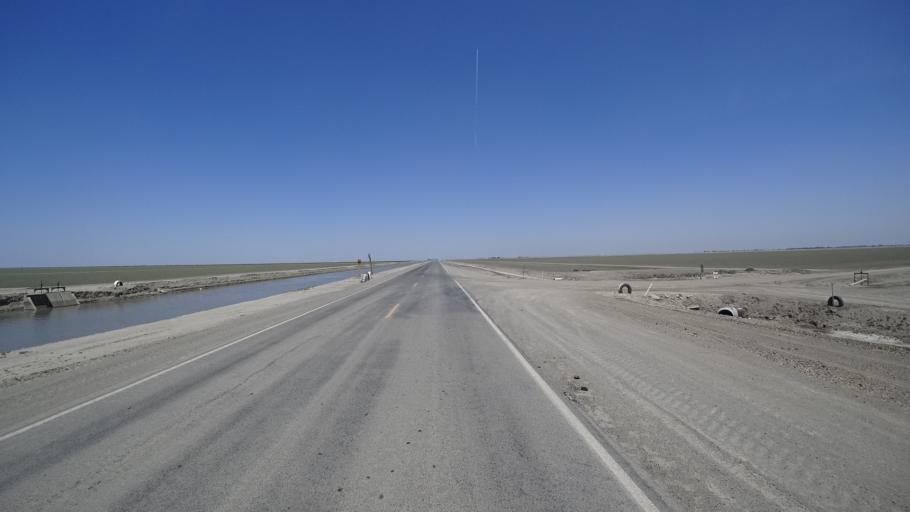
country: US
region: California
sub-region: Kings County
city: Corcoran
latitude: 36.0649
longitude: -119.6439
